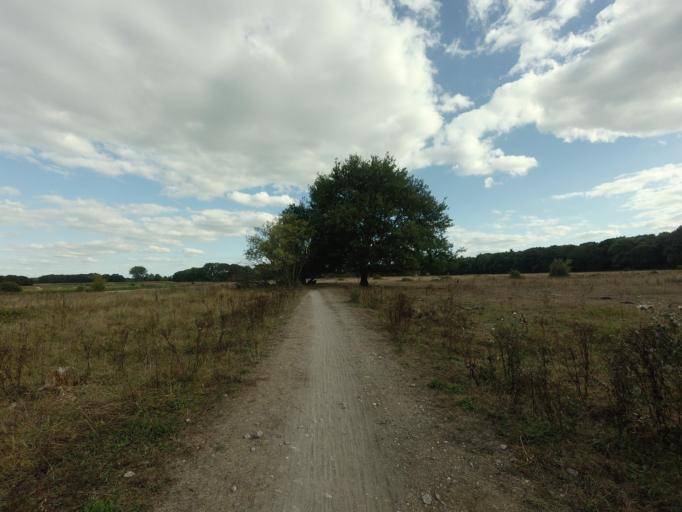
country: NL
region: North Brabant
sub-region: Gemeente Grave
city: Grave
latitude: 51.7249
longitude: 5.7477
